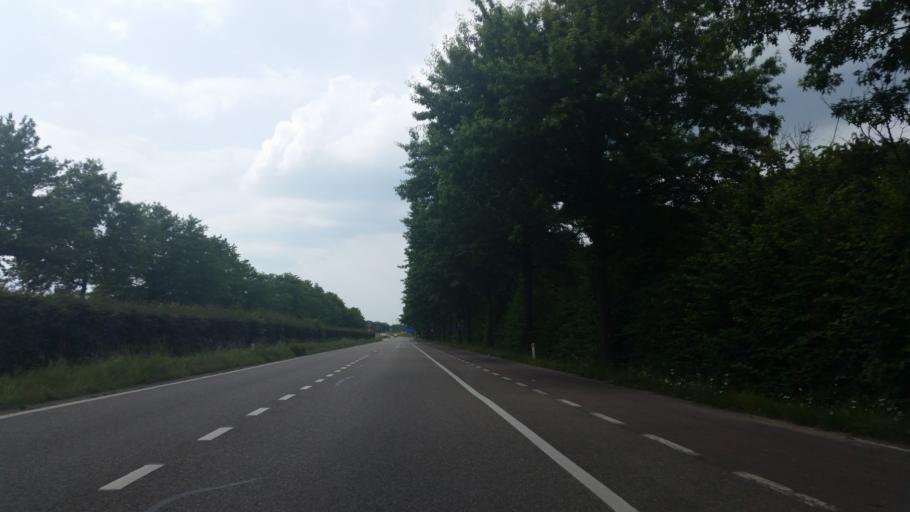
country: BE
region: Flanders
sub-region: Provincie Antwerpen
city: Geel
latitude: 51.1823
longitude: 4.9831
